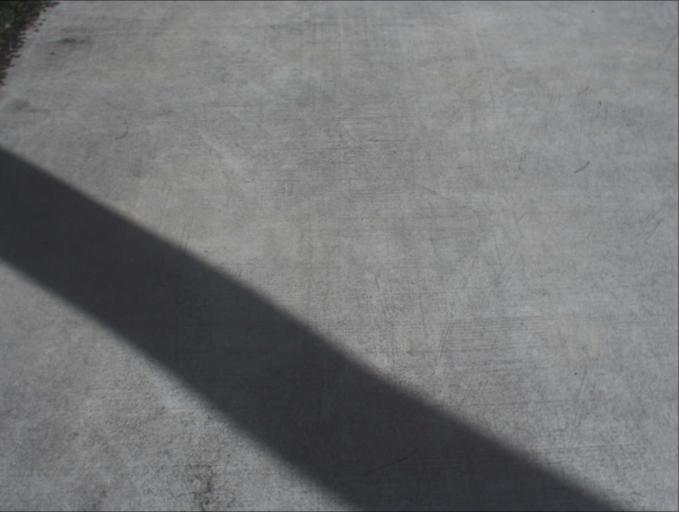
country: AU
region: Queensland
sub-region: Logan
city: Park Ridge South
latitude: -27.7398
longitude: 153.0266
